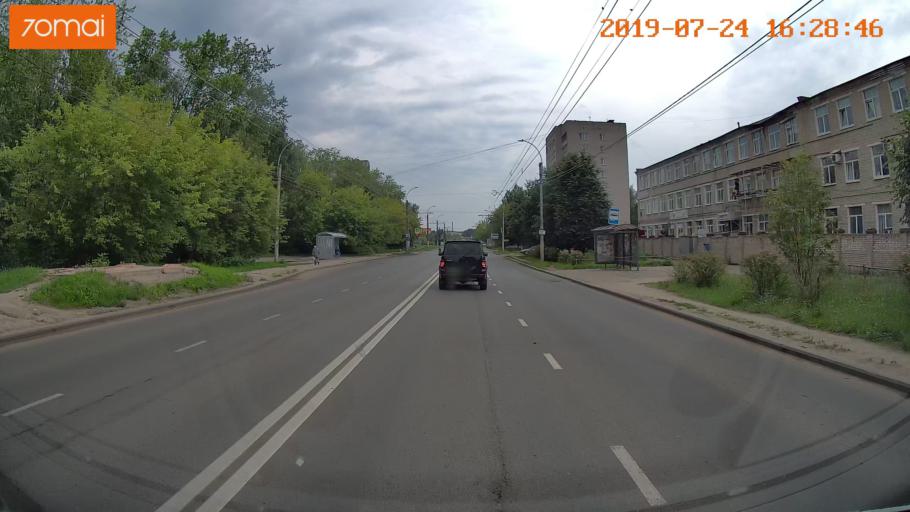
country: RU
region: Ivanovo
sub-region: Gorod Ivanovo
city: Ivanovo
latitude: 56.9683
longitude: 40.9631
